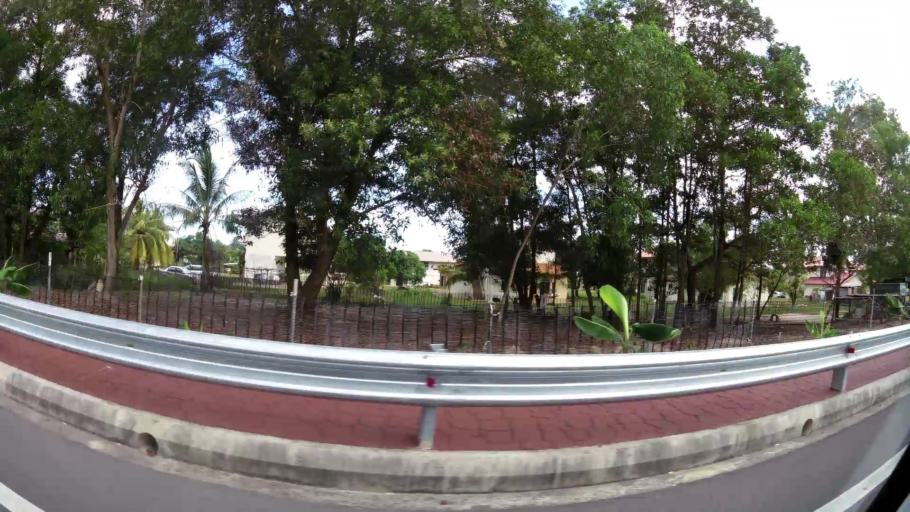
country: BN
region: Brunei and Muara
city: Bandar Seri Begawan
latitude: 4.9362
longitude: 114.8989
